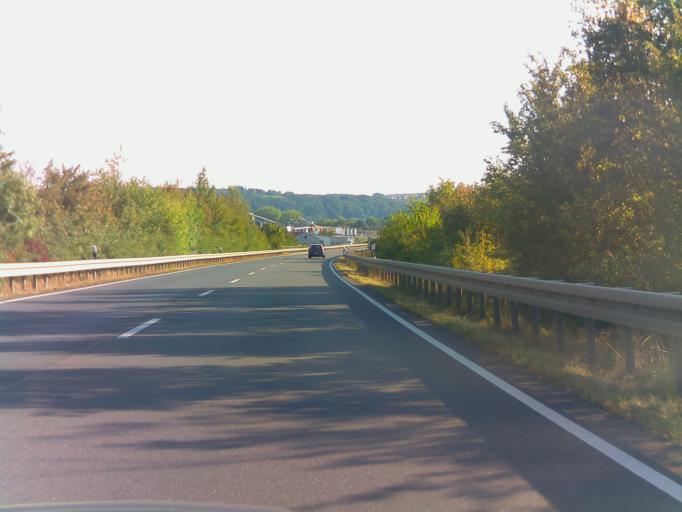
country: DE
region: Bavaria
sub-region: Regierungsbezirk Unterfranken
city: Marktsteft
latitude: 49.6929
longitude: 10.1437
